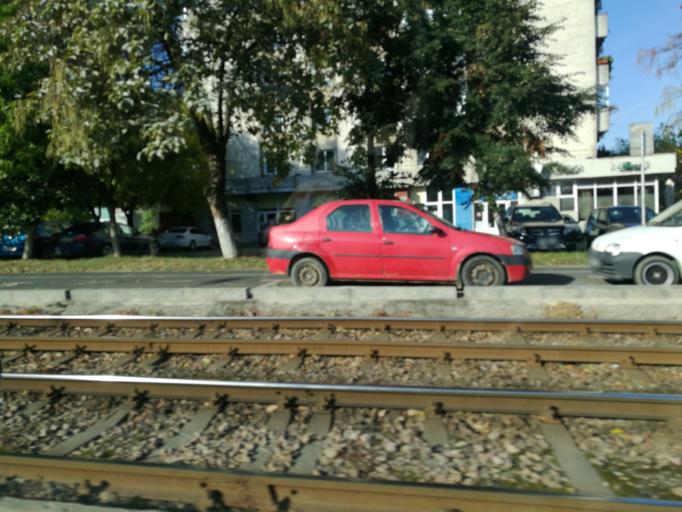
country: RO
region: Bihor
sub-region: Comuna Biharea
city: Oradea
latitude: 47.0435
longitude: 21.9418
